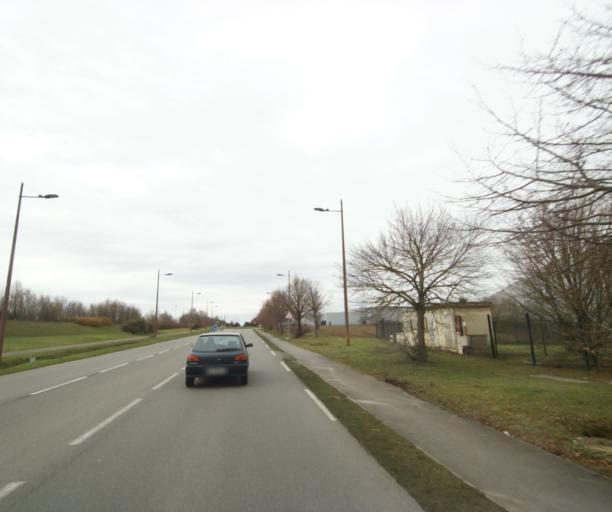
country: FR
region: Nord-Pas-de-Calais
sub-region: Departement du Nord
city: Onnaing
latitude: 50.3703
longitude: 3.6109
